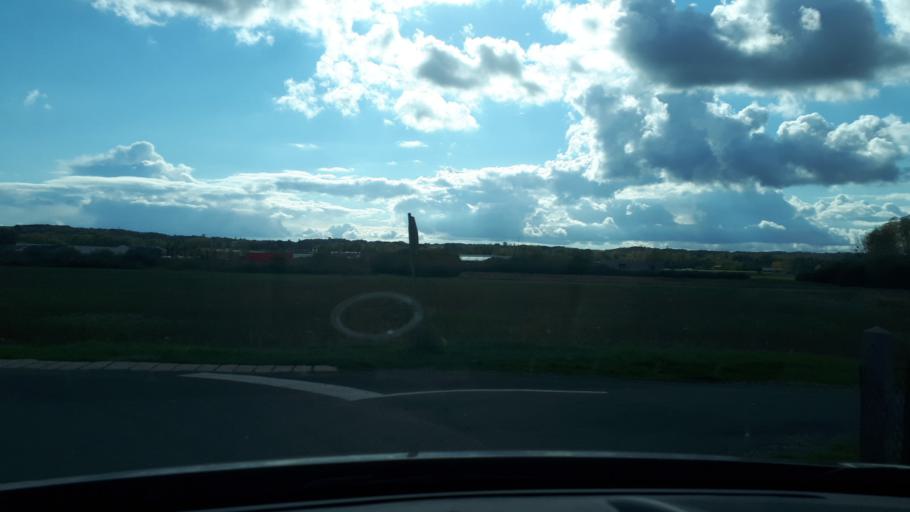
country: FR
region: Centre
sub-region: Departement du Loir-et-Cher
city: Saint-Aignan
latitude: 47.2903
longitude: 1.3763
